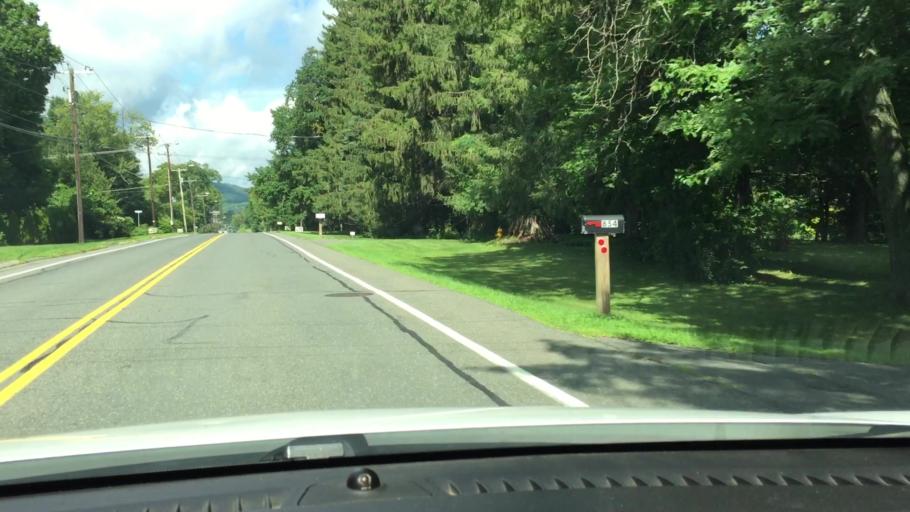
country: US
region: Massachusetts
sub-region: Berkshire County
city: Pittsfield
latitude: 42.4537
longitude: -73.2892
